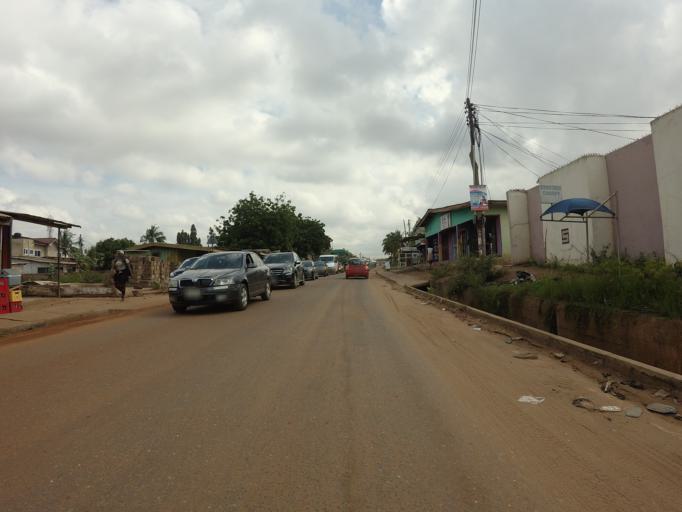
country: GH
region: Greater Accra
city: Teshi Old Town
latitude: 5.5951
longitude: -0.1214
